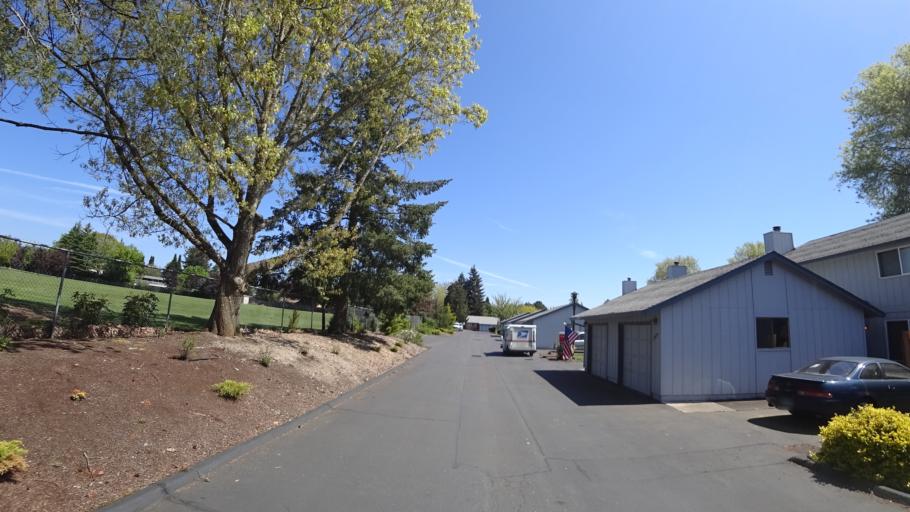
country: US
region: Oregon
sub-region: Washington County
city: Hillsboro
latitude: 45.5022
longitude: -122.9631
